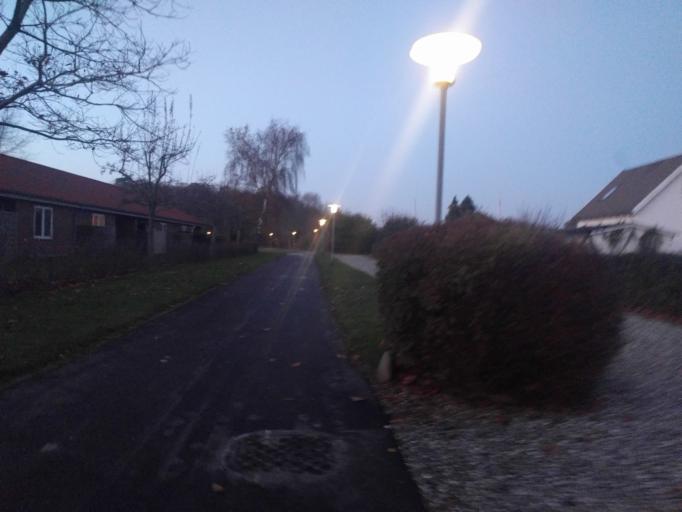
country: DK
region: South Denmark
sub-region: Fredericia Kommune
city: Snoghoj
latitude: 55.5381
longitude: 9.7242
